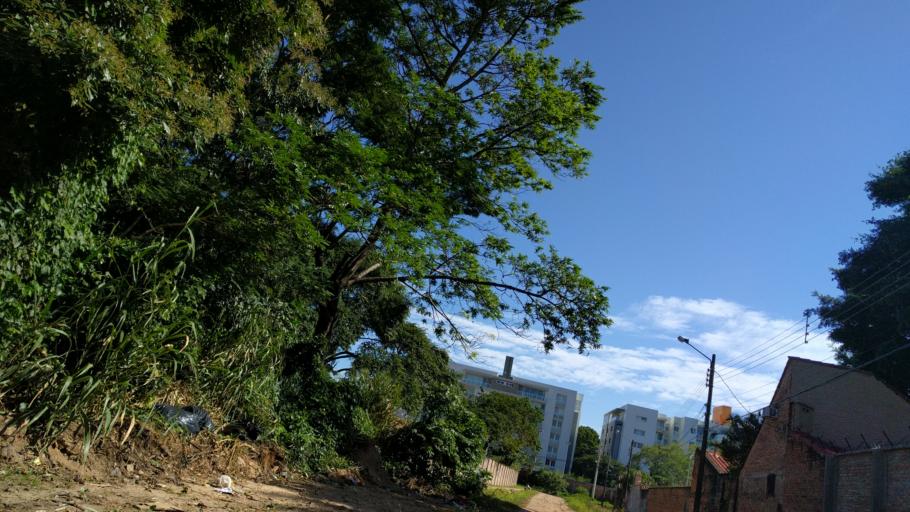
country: BO
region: Santa Cruz
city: Santa Cruz de la Sierra
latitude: -17.7973
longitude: -63.2212
